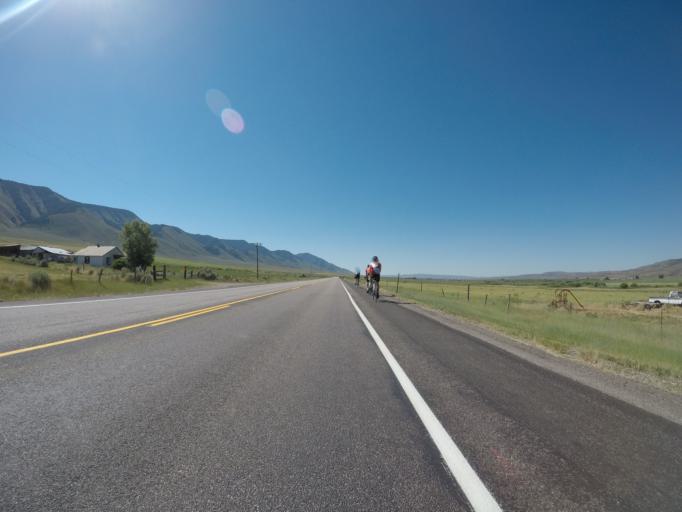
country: US
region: Idaho
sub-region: Bear Lake County
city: Montpelier
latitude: 42.3566
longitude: -111.0491
